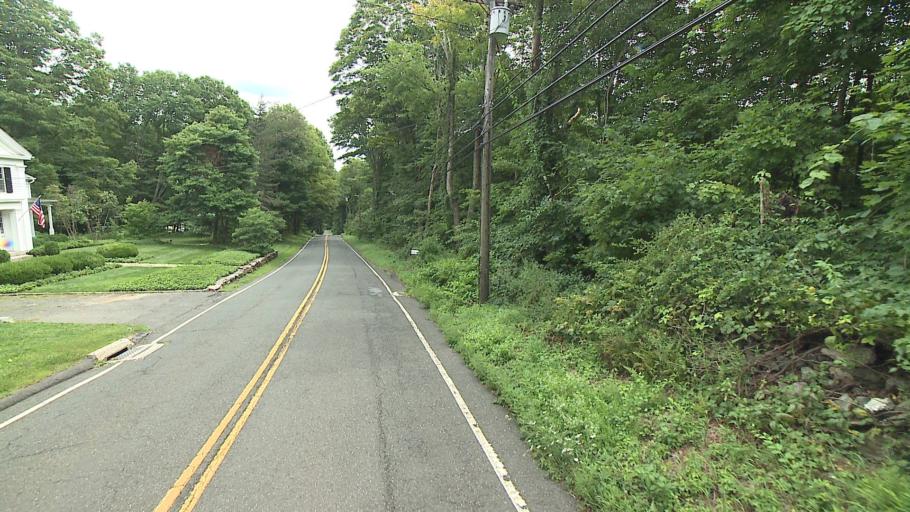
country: US
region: Connecticut
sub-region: Litchfield County
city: Woodbury
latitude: 41.5600
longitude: -73.2865
